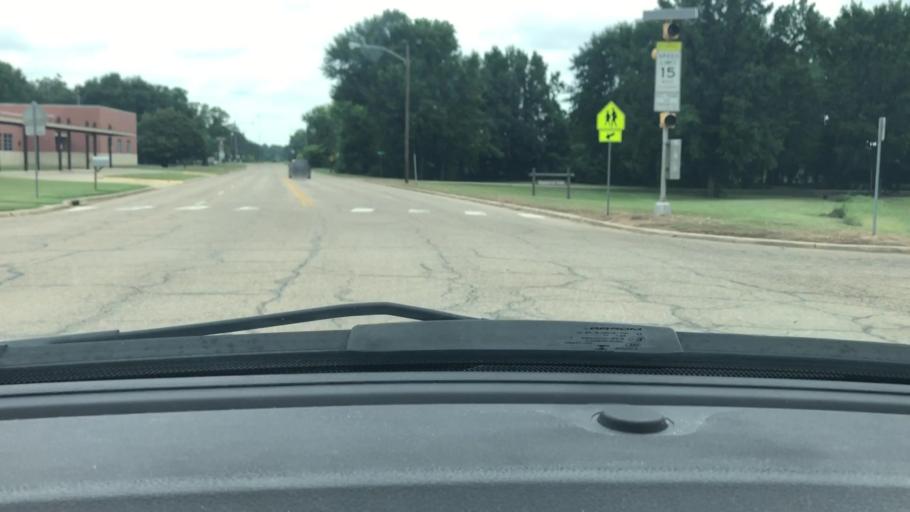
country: US
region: Texas
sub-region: Bowie County
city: Wake Village
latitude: 33.4055
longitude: -94.0790
